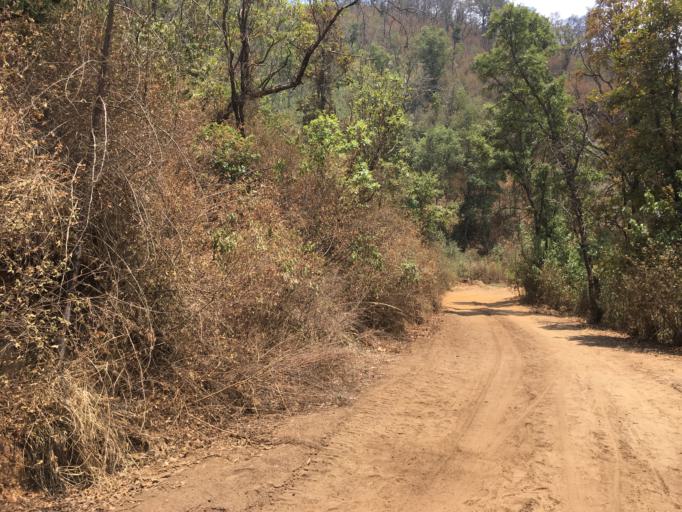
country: MX
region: Michoacan
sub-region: Patzcuaro
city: Santa Ana Chapitiro
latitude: 19.5161
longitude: -101.6421
